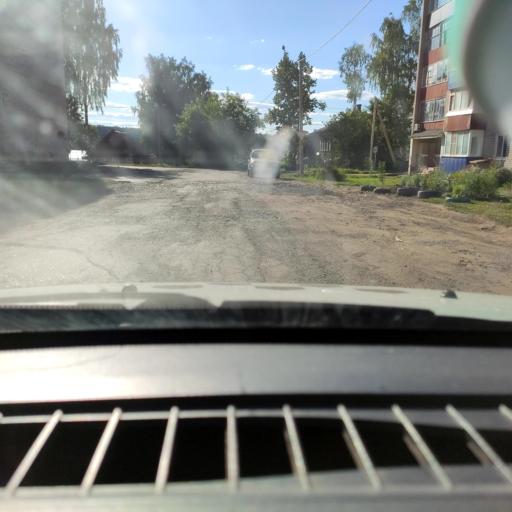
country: RU
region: Perm
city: Ocher
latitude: 57.8845
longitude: 54.7114
